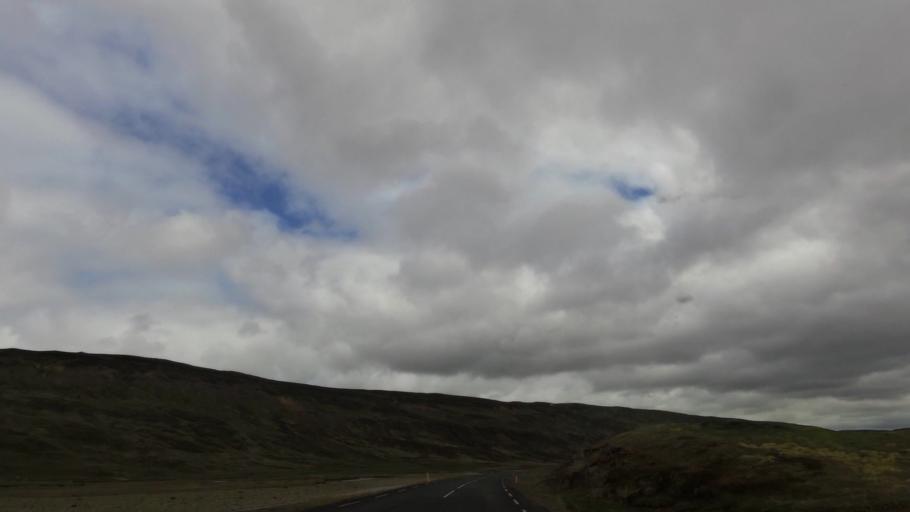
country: IS
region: West
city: Stykkisholmur
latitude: 65.7627
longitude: -21.8398
